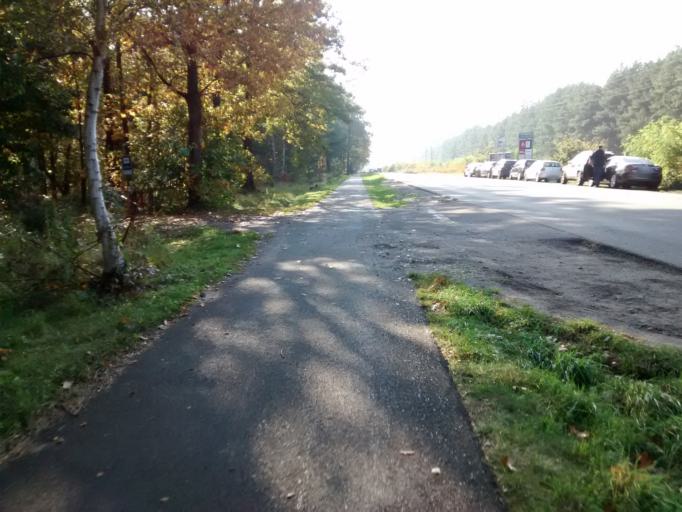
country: DE
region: Brandenburg
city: Hennigsdorf
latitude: 52.6482
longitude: 13.2362
